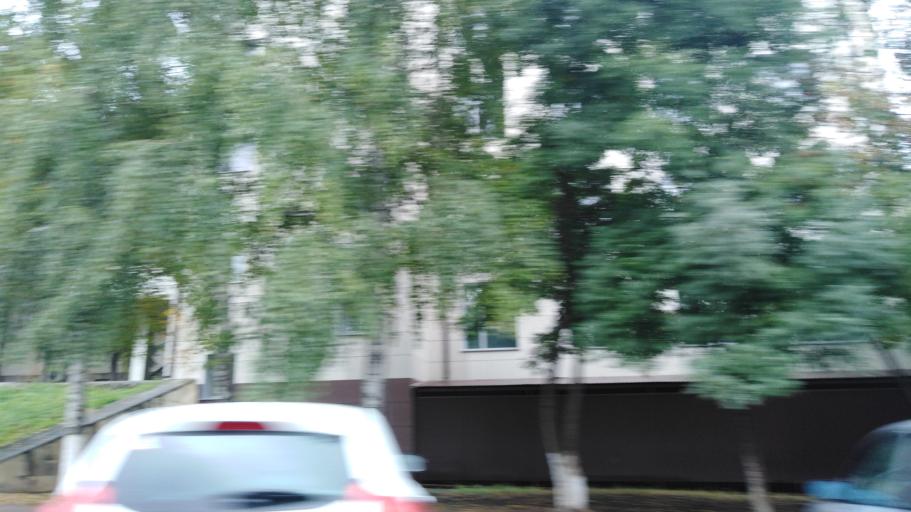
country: RU
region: Stavropol'skiy
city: Yessentukskaya
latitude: 44.0484
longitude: 42.8959
